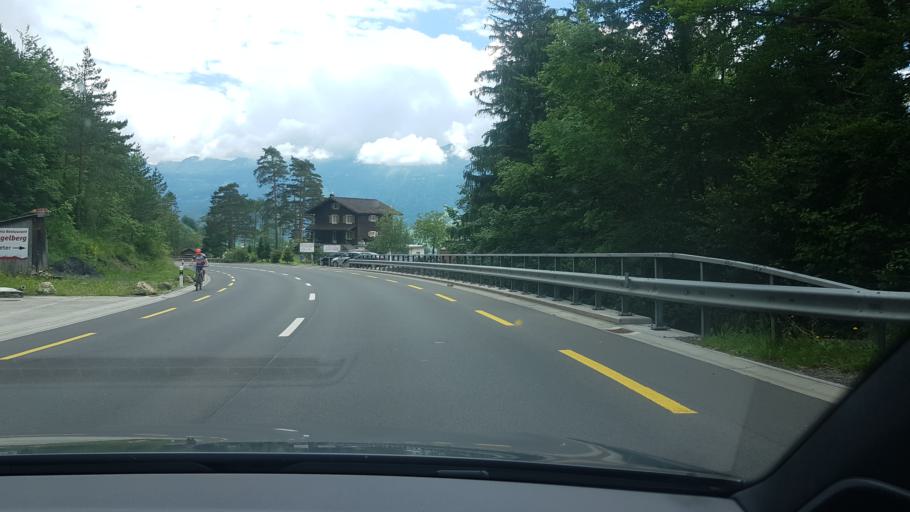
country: CH
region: Schwyz
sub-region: Bezirk Schwyz
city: Steinen
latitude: 47.0577
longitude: 8.6208
